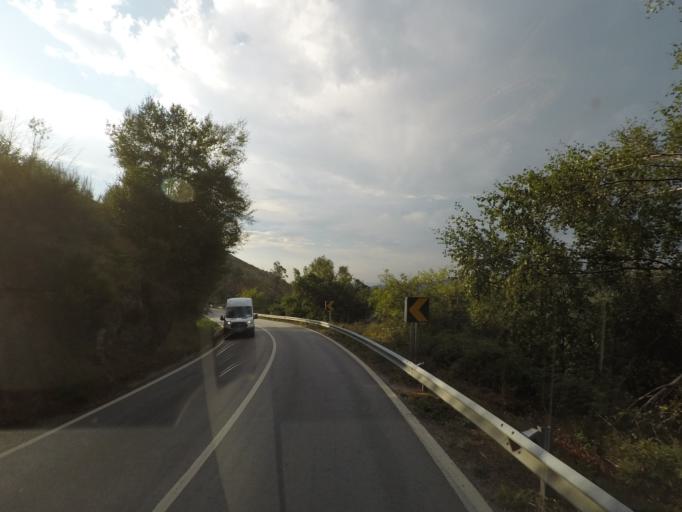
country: PT
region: Porto
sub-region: Baiao
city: Valadares
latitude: 41.1991
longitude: -7.9540
